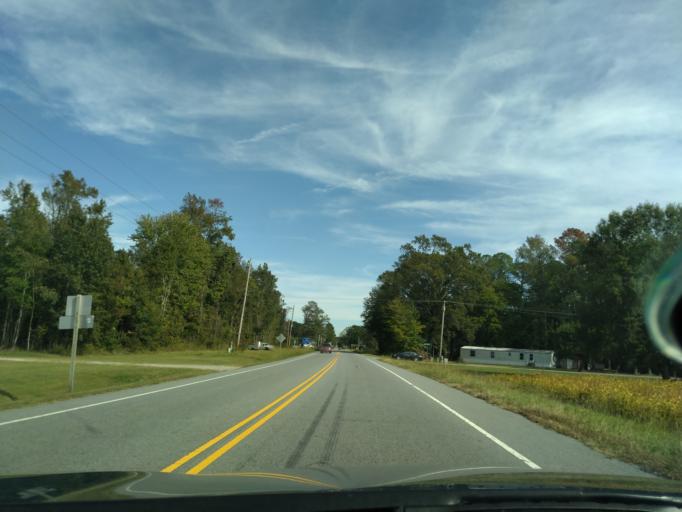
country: US
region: North Carolina
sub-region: Beaufort County
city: River Road
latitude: 35.5121
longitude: -76.9068
